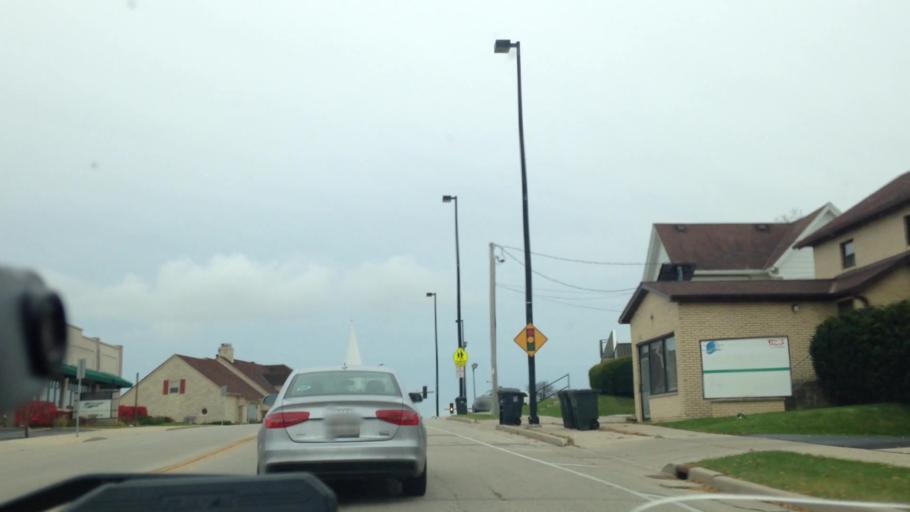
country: US
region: Wisconsin
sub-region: Waukesha County
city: Menomonee Falls
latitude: 43.1821
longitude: -88.1209
